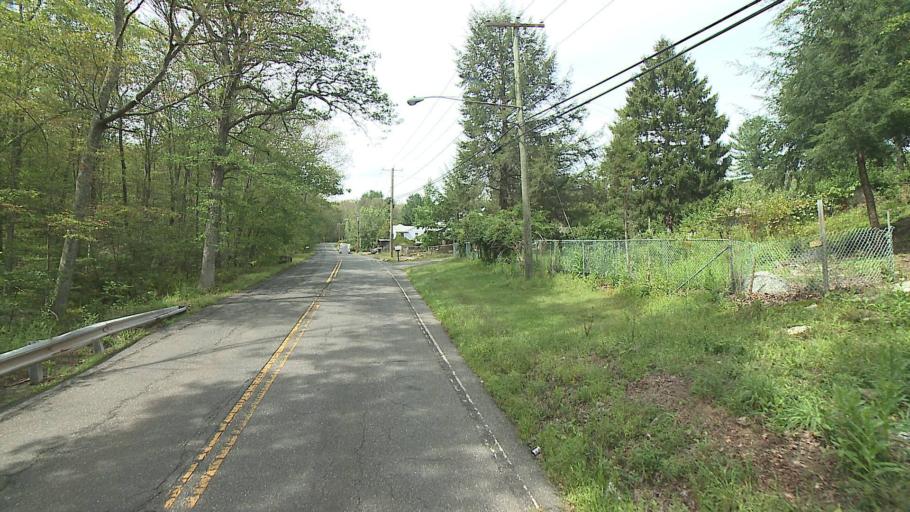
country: US
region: Connecticut
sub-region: Litchfield County
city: Oakville
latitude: 41.6173
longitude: -73.0476
